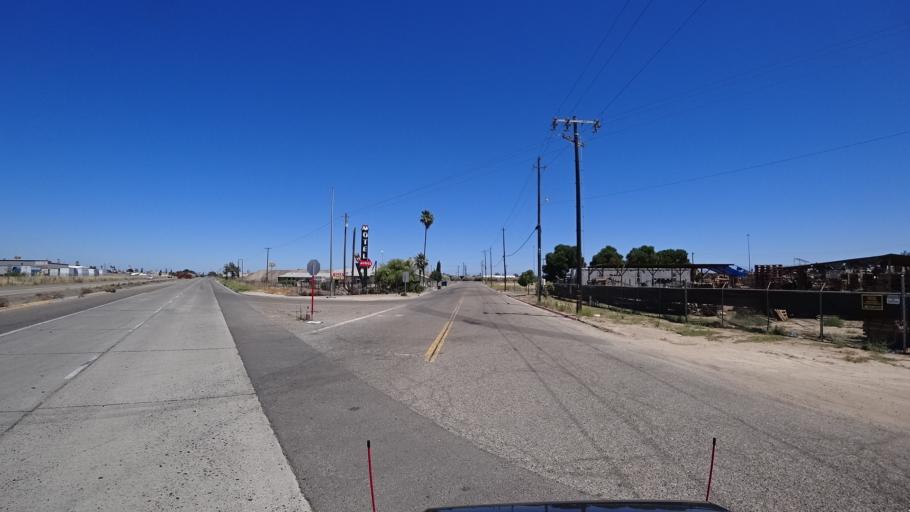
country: US
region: California
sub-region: Fresno County
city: Fresno
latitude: 36.7022
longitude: -119.7637
